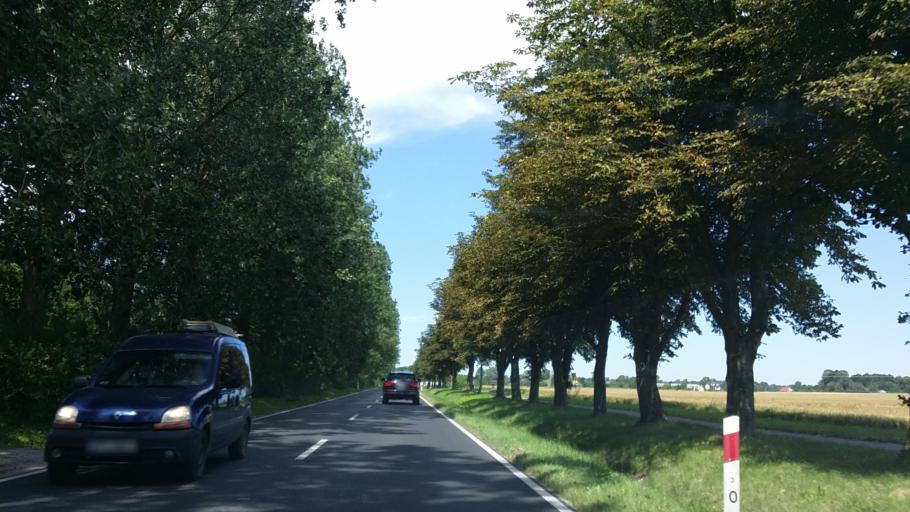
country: PL
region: West Pomeranian Voivodeship
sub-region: Powiat koszalinski
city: Mielno
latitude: 54.2324
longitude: 16.0737
